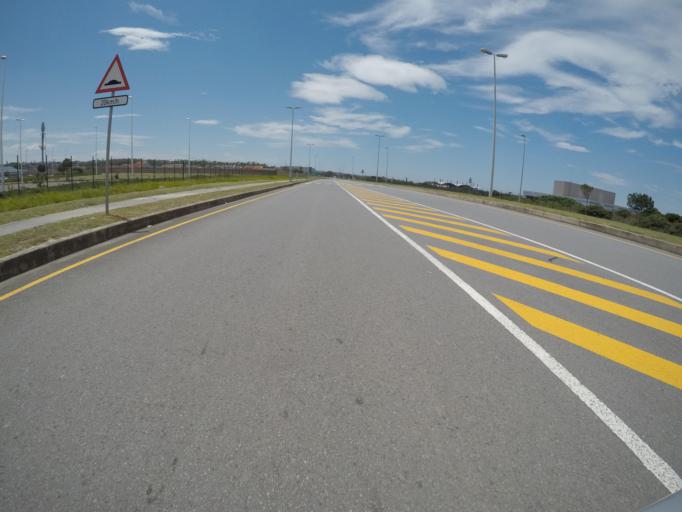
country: ZA
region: Eastern Cape
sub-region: Buffalo City Metropolitan Municipality
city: East London
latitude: -33.0510
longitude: 27.8488
